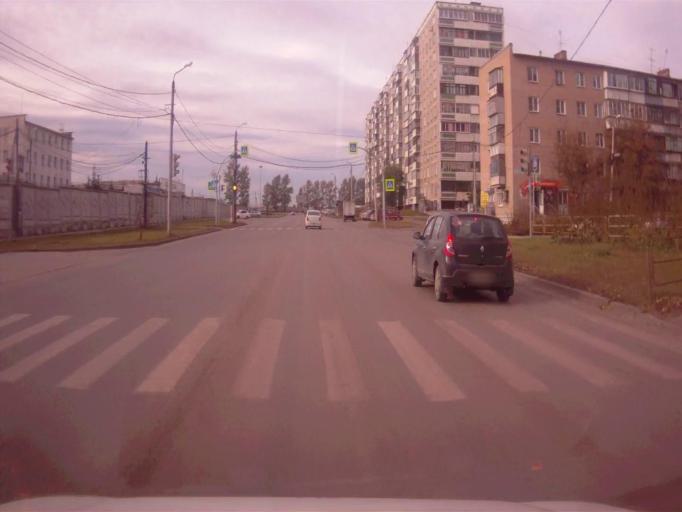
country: RU
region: Chelyabinsk
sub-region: Gorod Chelyabinsk
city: Chelyabinsk
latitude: 55.1172
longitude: 61.4232
